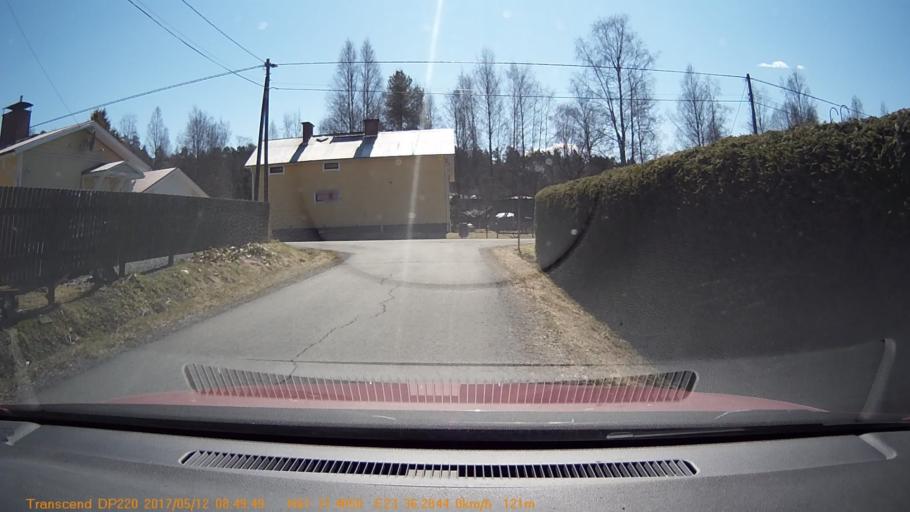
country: FI
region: Pirkanmaa
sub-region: Tampere
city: Yloejaervi
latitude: 61.5234
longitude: 23.6048
